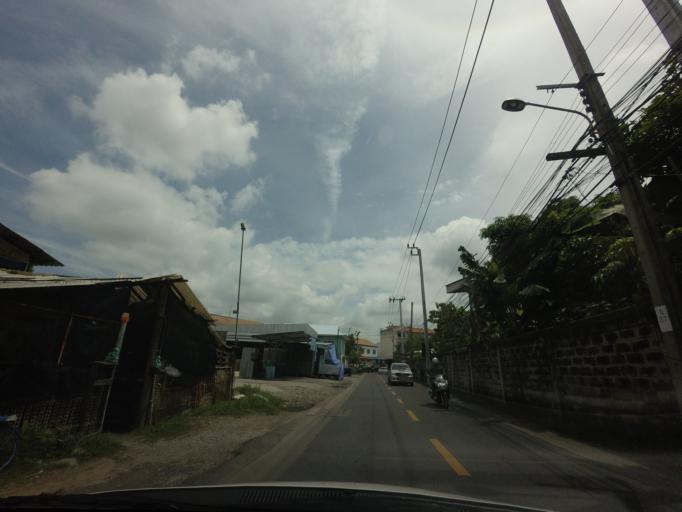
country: TH
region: Bangkok
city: Thung Khru
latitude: 13.6475
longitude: 100.5132
